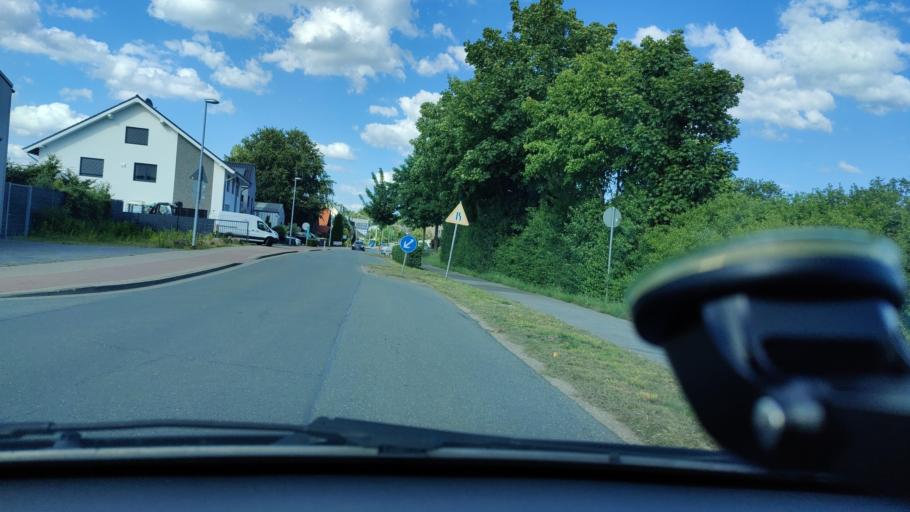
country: DE
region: North Rhine-Westphalia
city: Rheinberg
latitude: 51.5432
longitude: 6.5730
